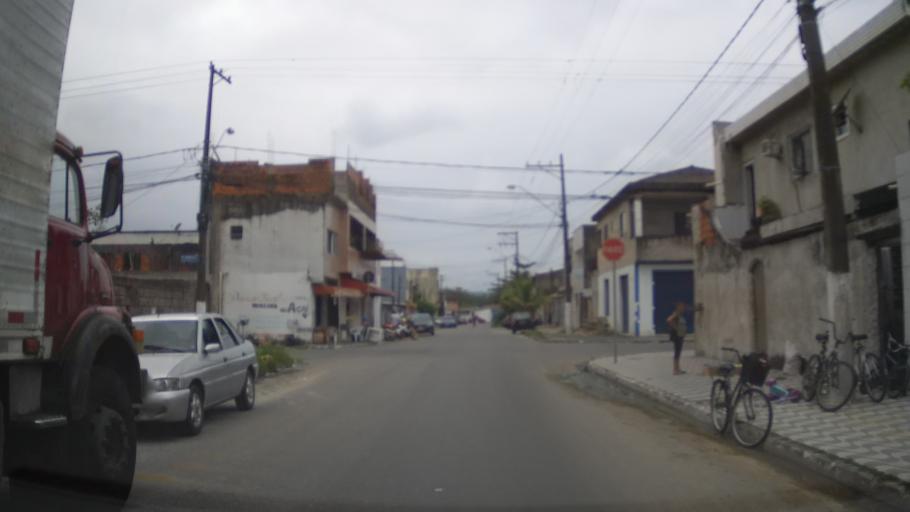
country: BR
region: Sao Paulo
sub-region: Praia Grande
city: Praia Grande
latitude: -23.9967
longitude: -46.4504
